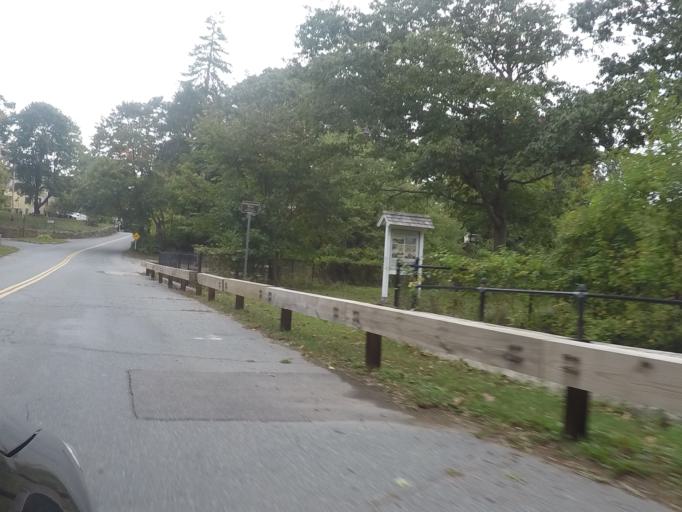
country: US
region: Massachusetts
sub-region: Bristol County
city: Smith Mills
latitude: 41.5709
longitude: -71.0046
